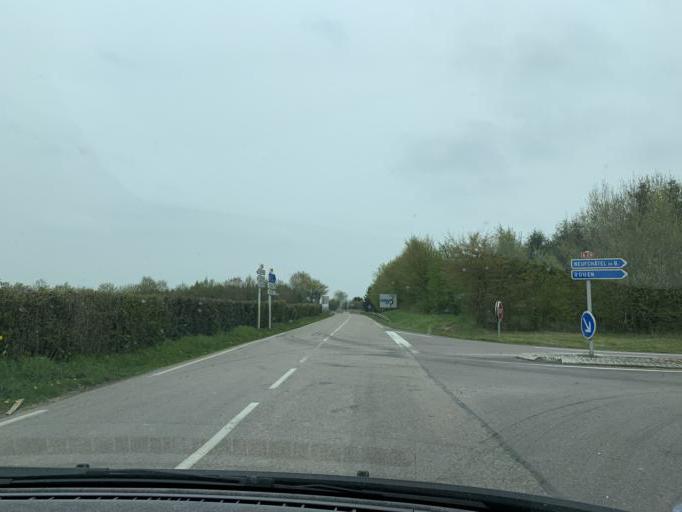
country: FR
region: Haute-Normandie
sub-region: Departement de la Seine-Maritime
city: Foucarmont
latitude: 49.8315
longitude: 1.5236
